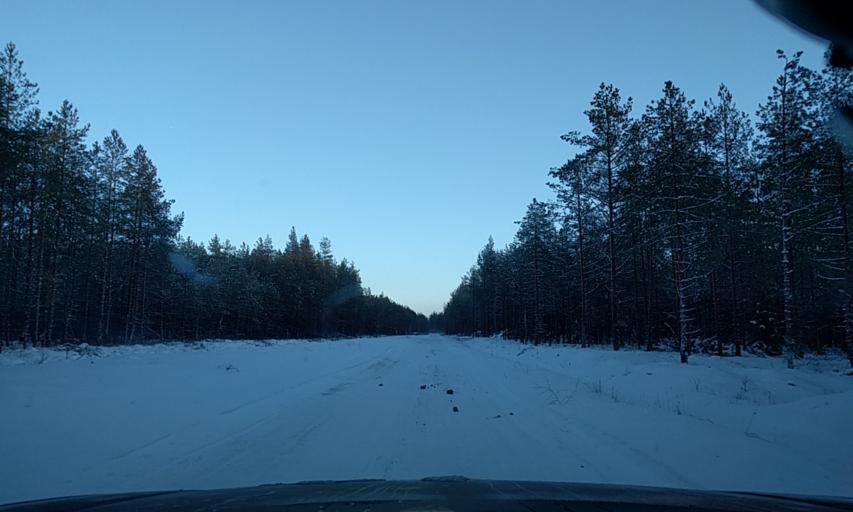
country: EE
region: Harju
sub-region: Saku vald
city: Saku
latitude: 59.3206
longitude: 24.6716
